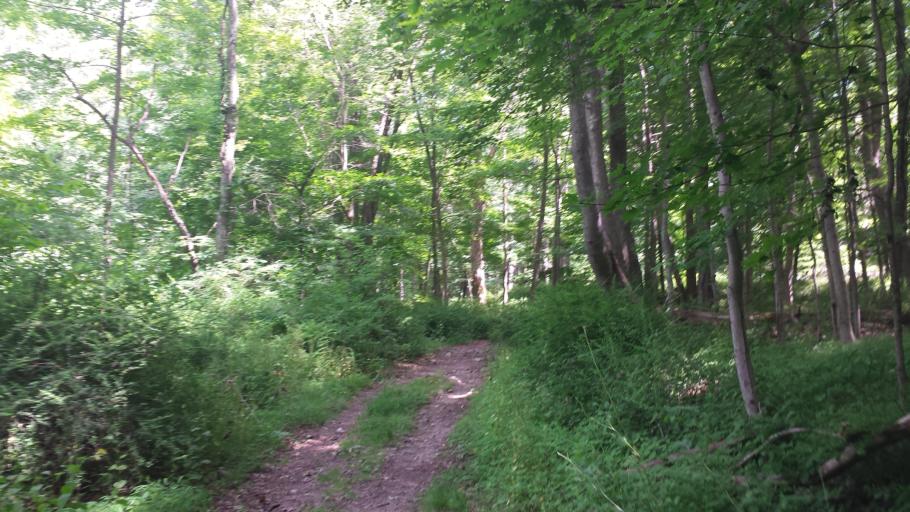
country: US
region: New York
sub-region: Westchester County
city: Pound Ridge
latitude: 41.2459
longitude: -73.5897
